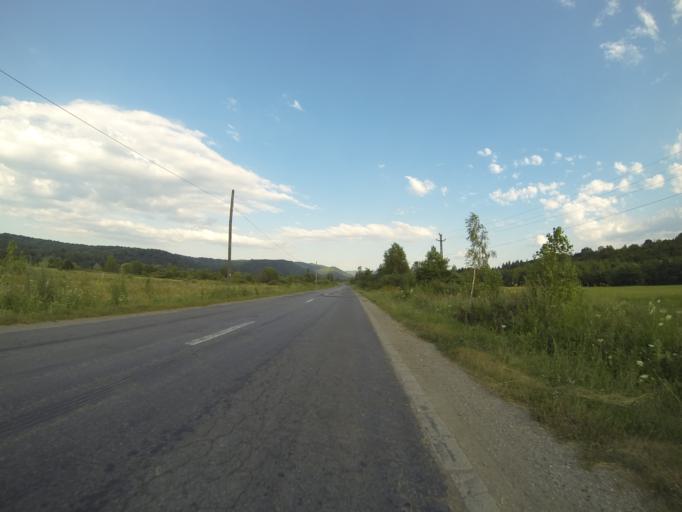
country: RO
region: Brasov
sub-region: Comuna Sinca Veche
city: Sinca Veche
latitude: 45.7448
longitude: 25.1976
